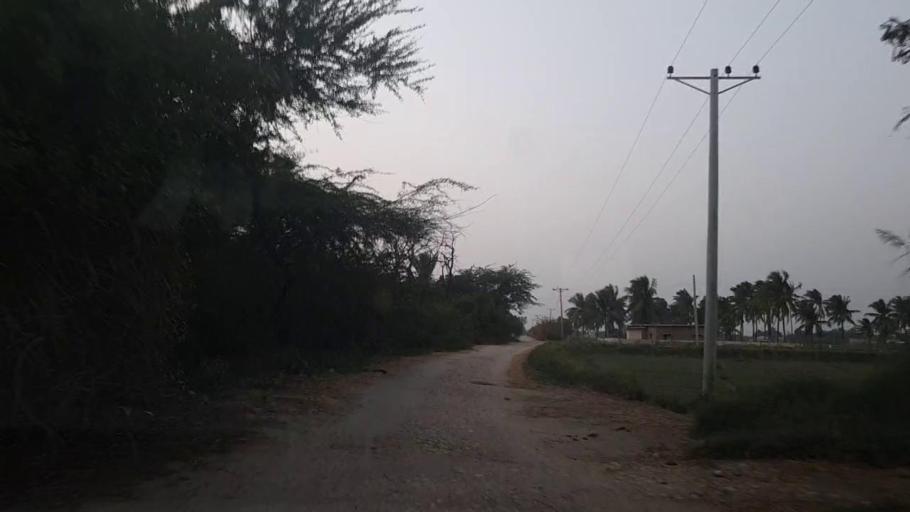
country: PK
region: Sindh
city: Mirpur Sakro
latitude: 24.5902
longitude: 67.7810
